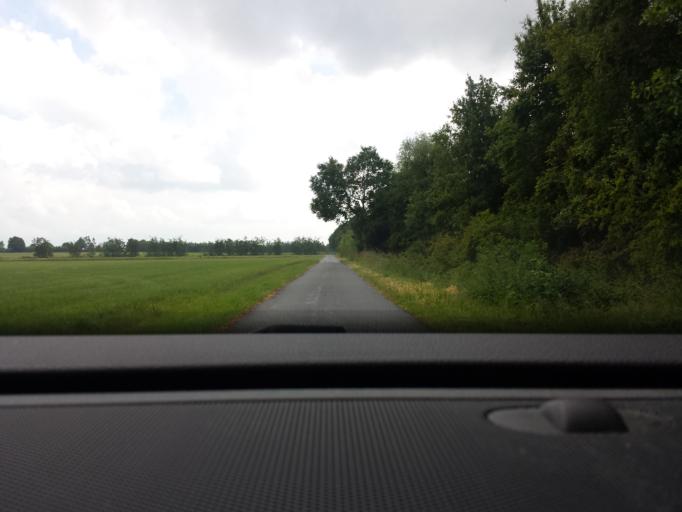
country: NL
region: Gelderland
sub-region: Berkelland
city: Eibergen
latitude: 52.0697
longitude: 6.7254
